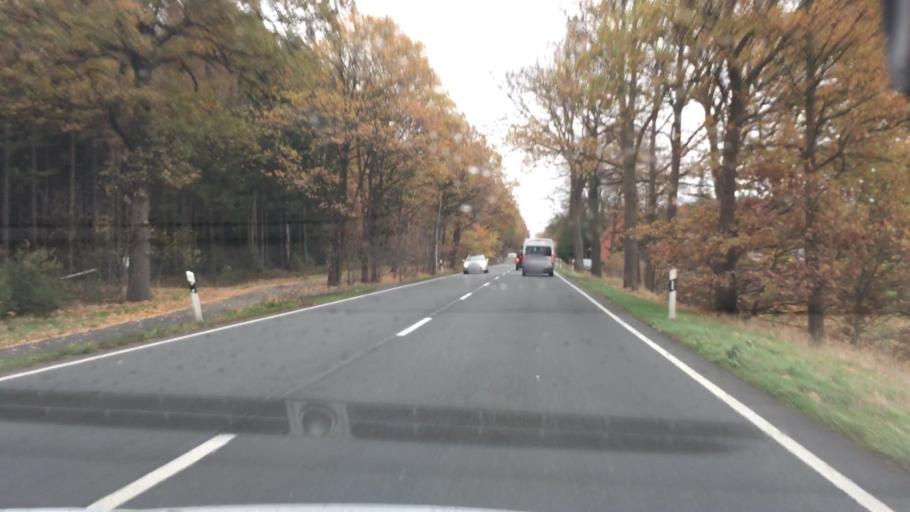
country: DE
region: Lower Saxony
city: Pennigsehl
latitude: 52.6626
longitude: 9.0453
